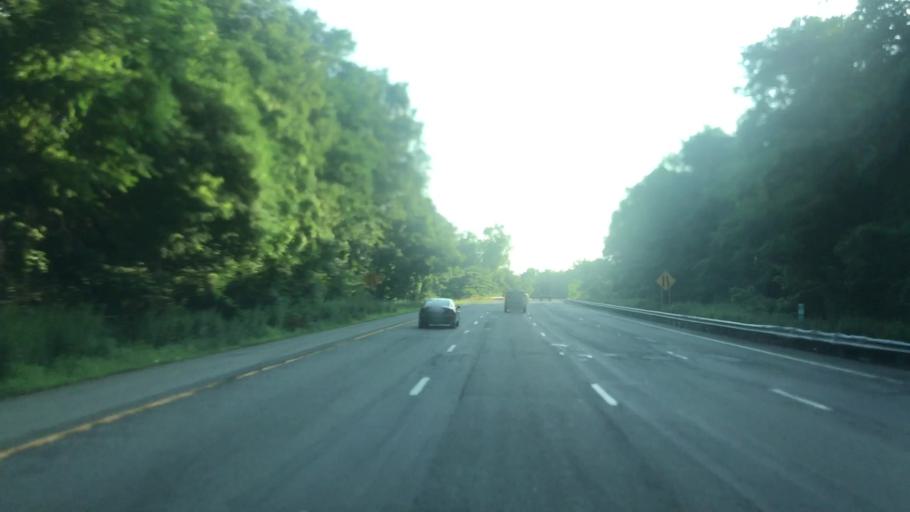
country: US
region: New York
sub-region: Westchester County
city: Purchase
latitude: 41.0279
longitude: -73.7273
